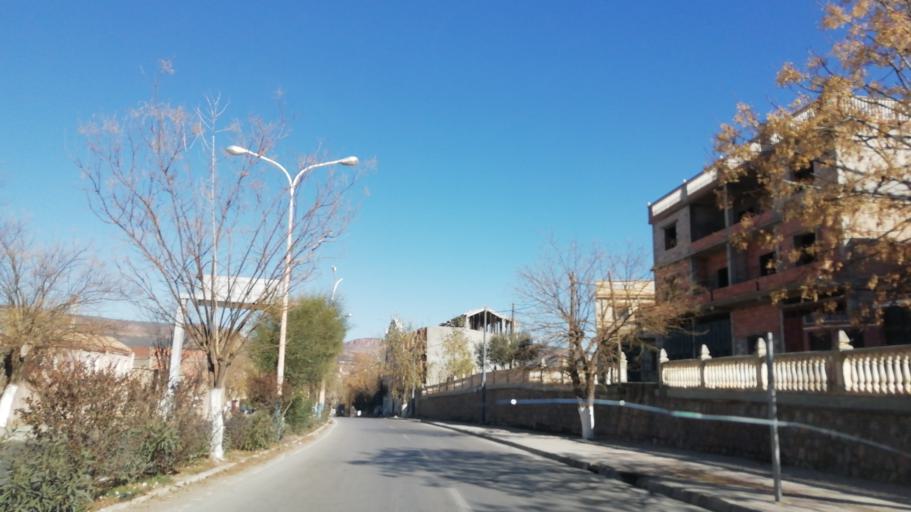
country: DZ
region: Tlemcen
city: Sebdou
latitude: 34.6523
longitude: -1.3261
